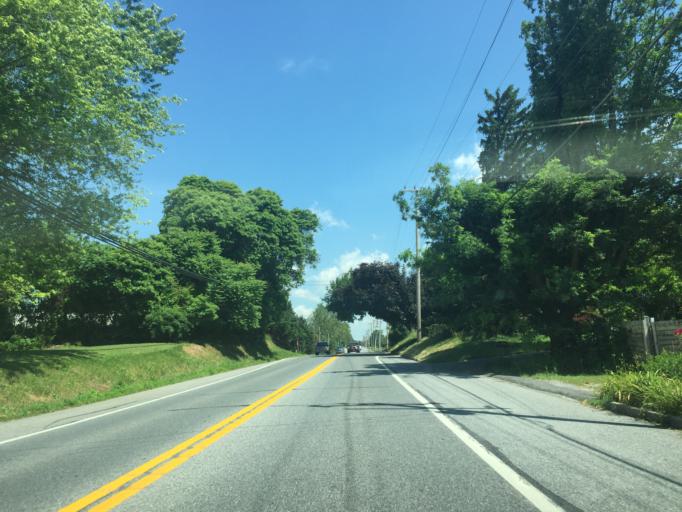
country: US
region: Maryland
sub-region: Baltimore County
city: Reisterstown
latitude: 39.4954
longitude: -76.8311
